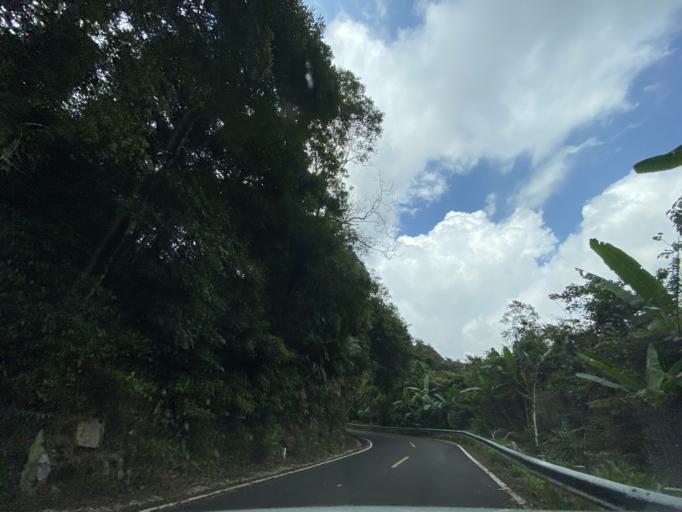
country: CN
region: Hainan
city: Diaoluoshan
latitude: 18.7065
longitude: 109.8823
